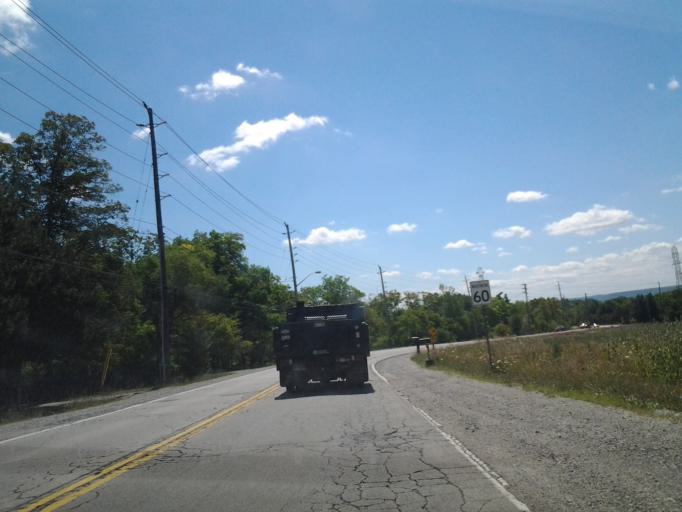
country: CA
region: Ontario
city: Hamilton
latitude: 43.3193
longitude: -79.8702
